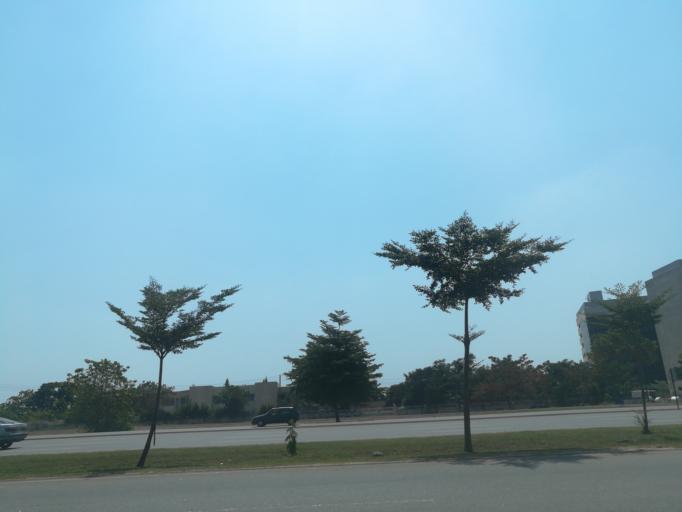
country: NG
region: Abuja Federal Capital Territory
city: Abuja
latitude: 9.0767
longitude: 7.4439
